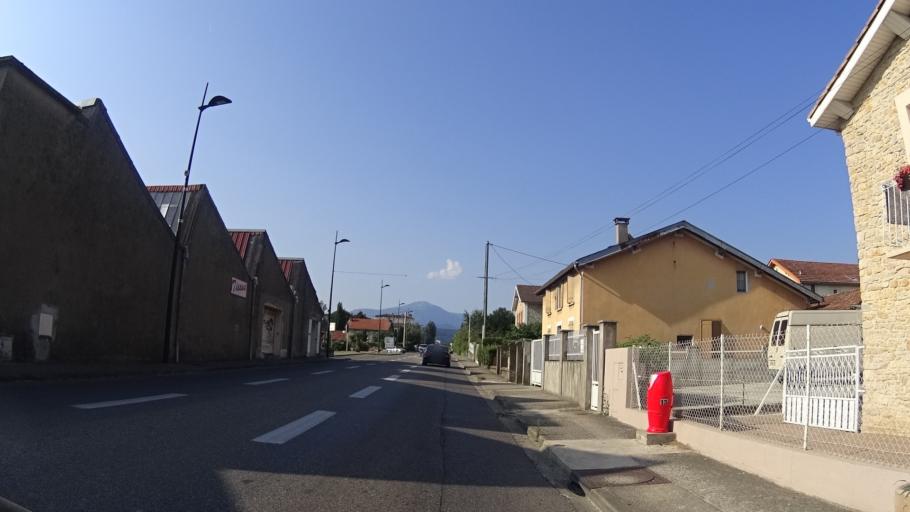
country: FR
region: Midi-Pyrenees
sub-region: Departement de l'Ariege
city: Lavelanet
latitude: 42.9699
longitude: 1.8662
